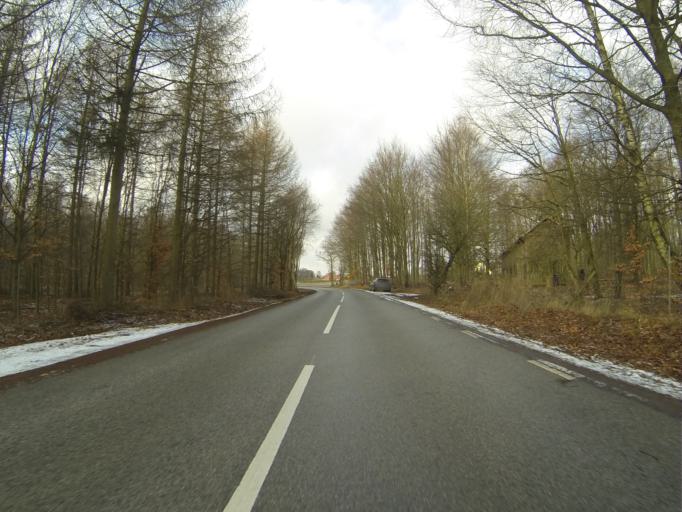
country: SE
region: Skane
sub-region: Svedala Kommun
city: Svedala
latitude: 55.5371
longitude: 13.2769
